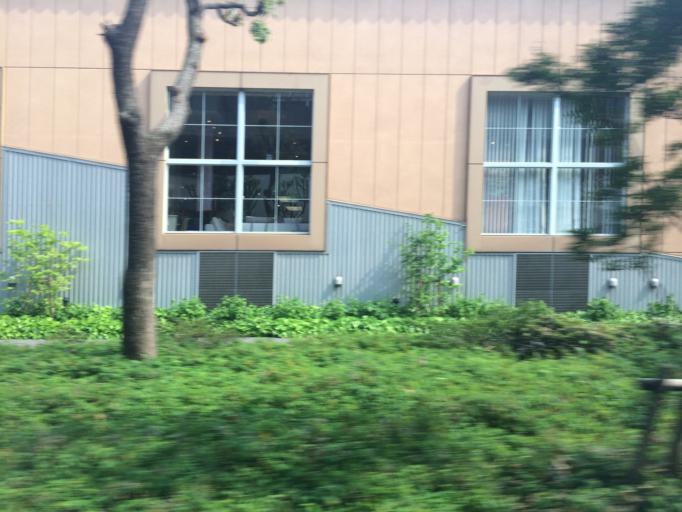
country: JP
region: Hyogo
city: Kobe
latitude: 34.7092
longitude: 135.2412
